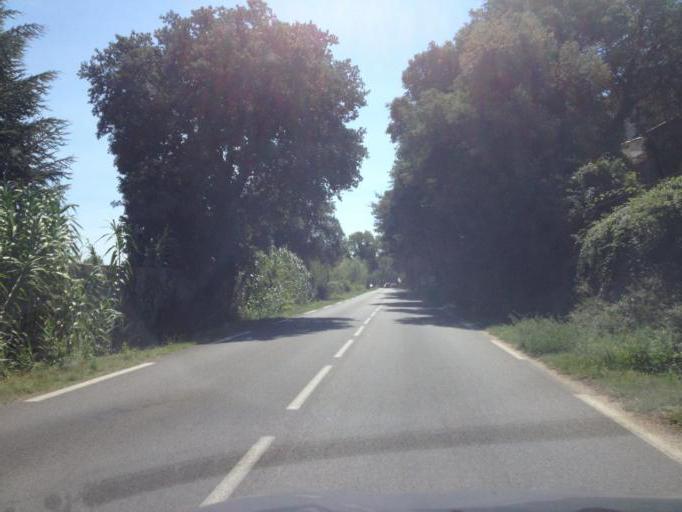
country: FR
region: Languedoc-Roussillon
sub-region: Departement du Gard
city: Sauveterre
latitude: 44.0172
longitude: 4.7949
